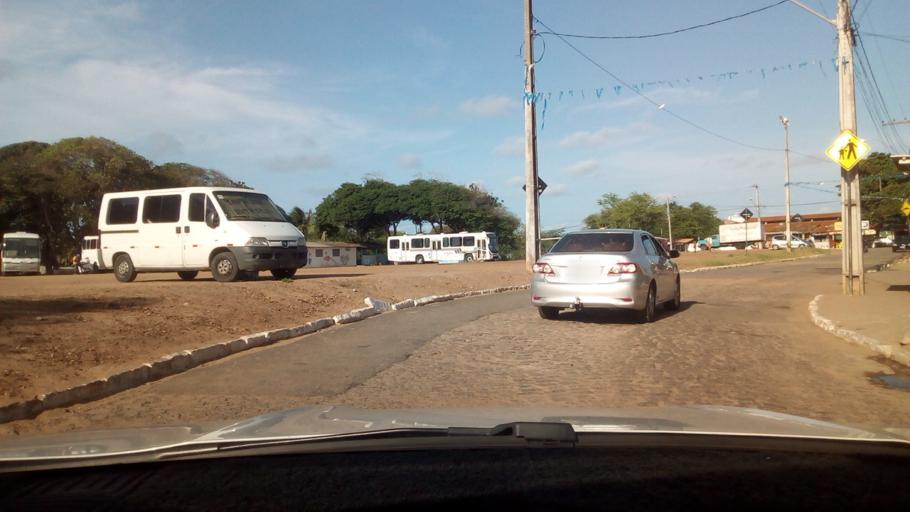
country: BR
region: Paraiba
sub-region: Joao Pessoa
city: Joao Pessoa
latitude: -7.1654
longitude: -34.7992
